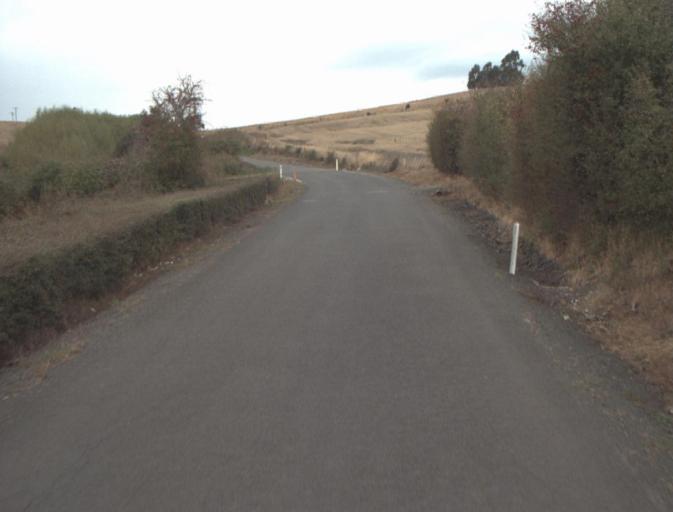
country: AU
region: Tasmania
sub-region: Northern Midlands
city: Evandale
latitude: -41.5267
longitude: 147.2461
